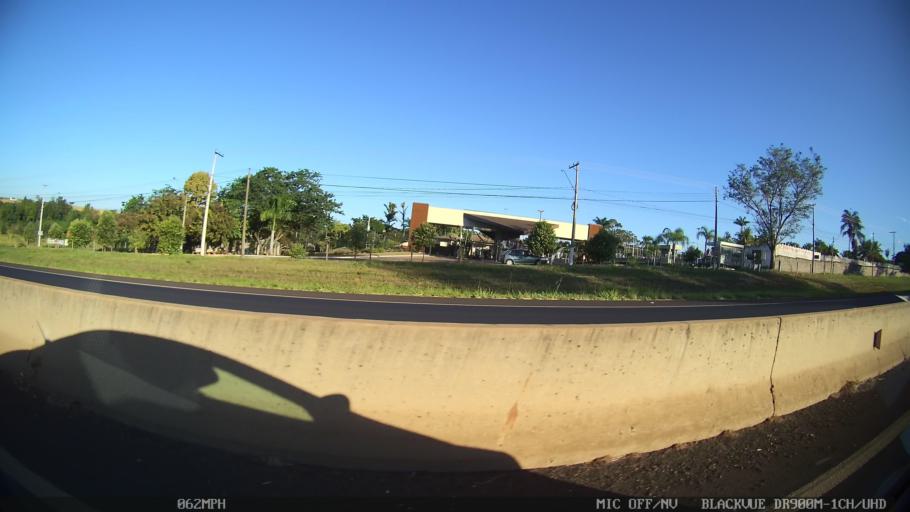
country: BR
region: Sao Paulo
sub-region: Guapiacu
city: Guapiacu
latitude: -20.7847
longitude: -49.2723
